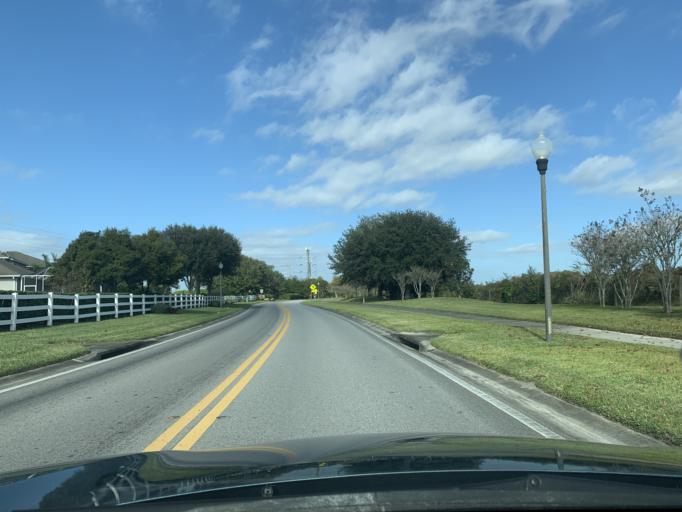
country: US
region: Florida
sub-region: Pasco County
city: Trinity
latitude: 28.1995
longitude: -82.6799
